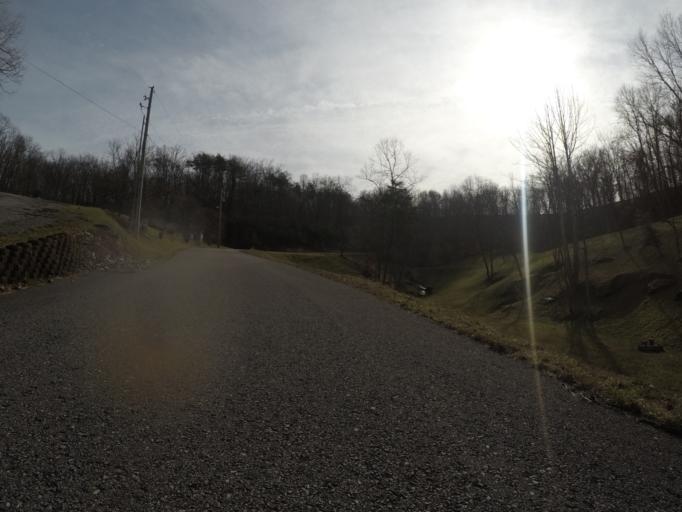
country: US
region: West Virginia
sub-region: Cabell County
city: Huntington
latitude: 38.3858
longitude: -82.3918
